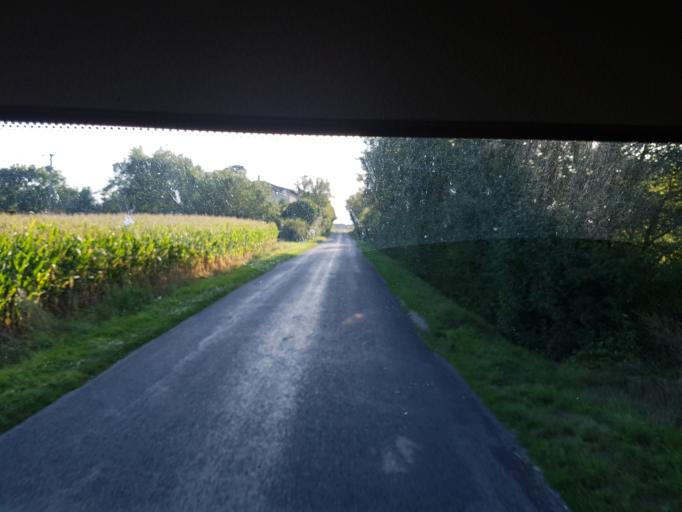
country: FR
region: Rhone-Alpes
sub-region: Departement de l'Ain
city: Villars-les-Dombes
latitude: 45.9641
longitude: 5.0558
